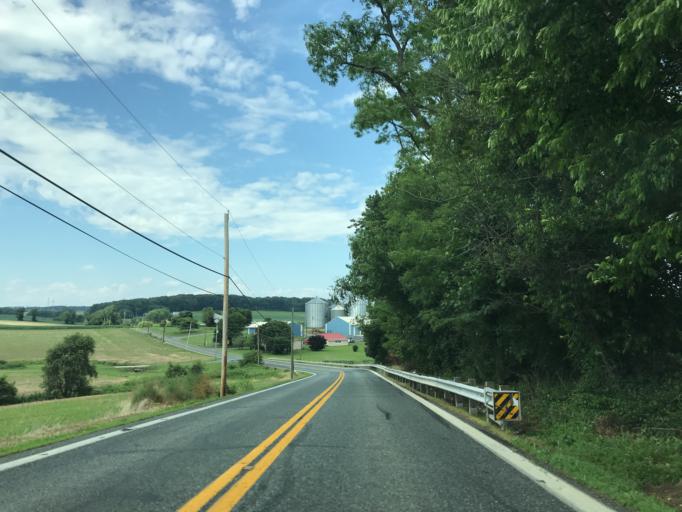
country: US
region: Pennsylvania
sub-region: York County
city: Susquehanna Trails
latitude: 39.6791
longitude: -76.4098
